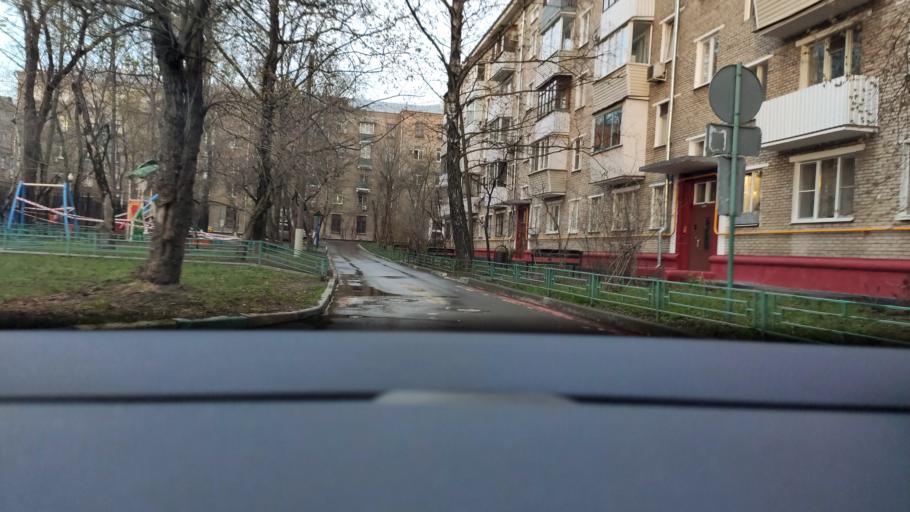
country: RU
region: Moscow
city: Ryazanskiy
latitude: 55.7559
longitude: 37.7735
